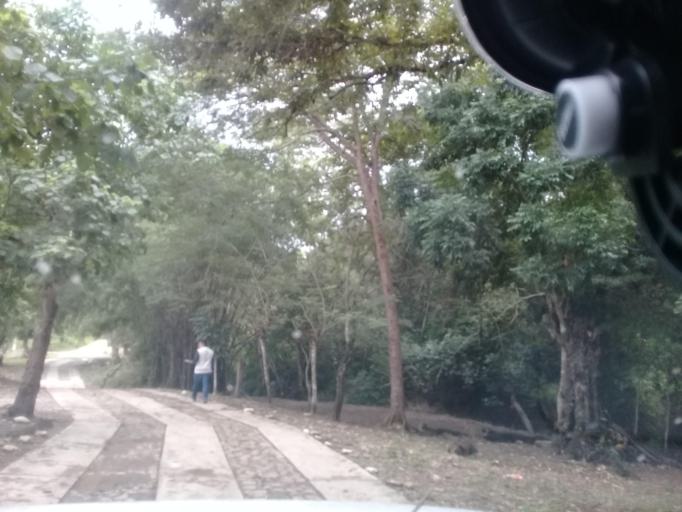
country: MX
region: Hidalgo
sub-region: Huejutla de Reyes
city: Chalahuiyapa
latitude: 21.1850
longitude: -98.3483
